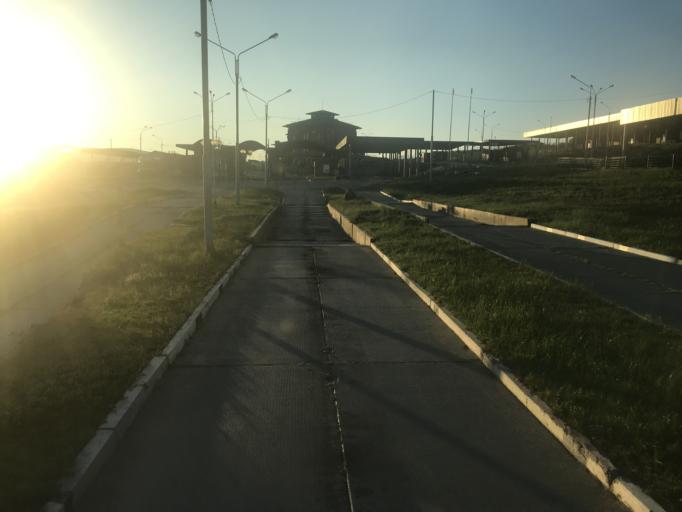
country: MN
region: Selenge
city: Altanbulag
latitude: 50.3244
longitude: 106.4886
